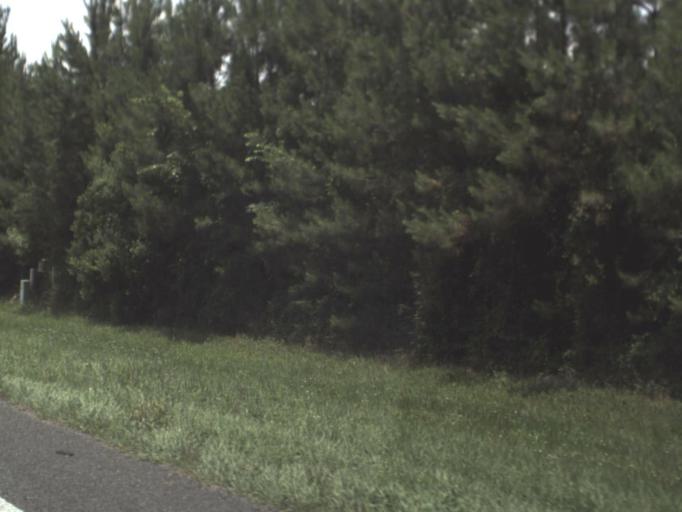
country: US
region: Florida
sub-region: Nassau County
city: Callahan
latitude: 30.5809
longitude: -81.8326
